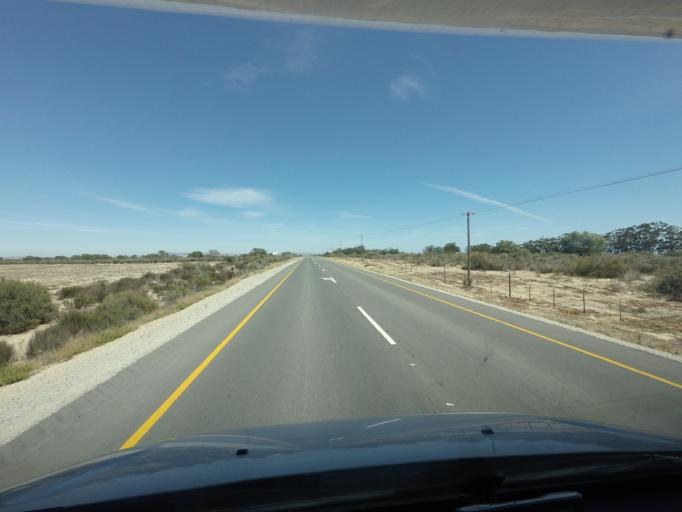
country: ZA
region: Western Cape
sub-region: West Coast District Municipality
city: Vredenburg
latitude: -32.7951
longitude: 18.2478
